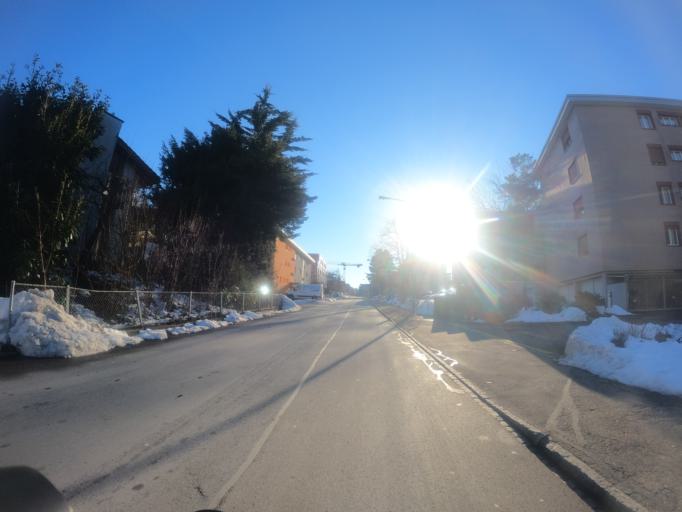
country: CH
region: Zurich
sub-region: Bezirk Affoltern
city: Affoltern / Oberdorf
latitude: 47.2804
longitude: 8.4489
